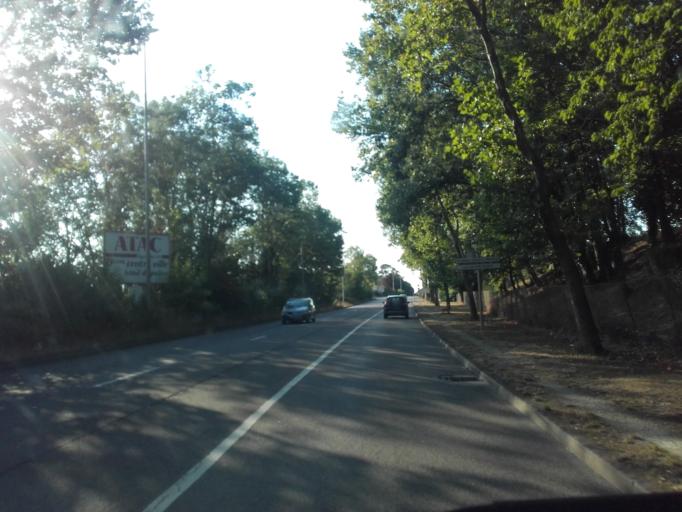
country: FR
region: Bourgogne
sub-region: Departement de l'Yonne
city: Auxerre
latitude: 47.7903
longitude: 3.5916
